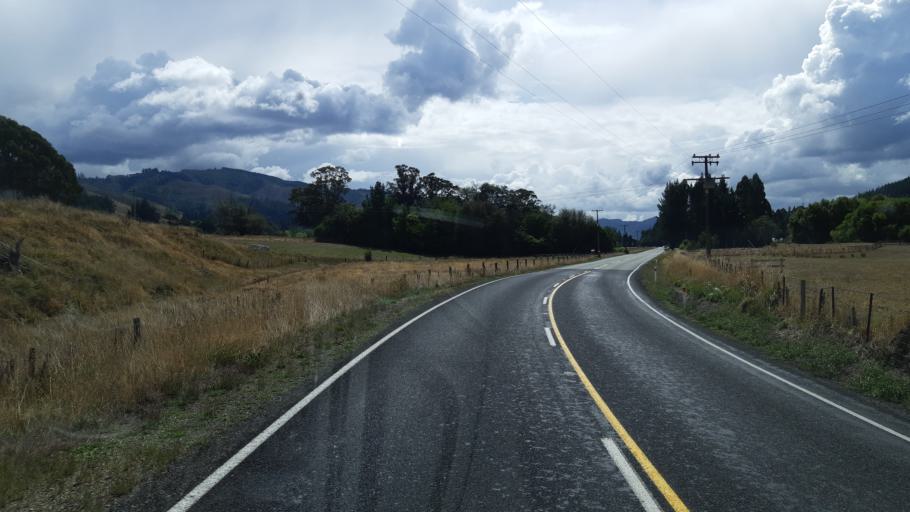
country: NZ
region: Tasman
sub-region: Tasman District
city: Wakefield
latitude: -41.4793
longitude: 172.8024
